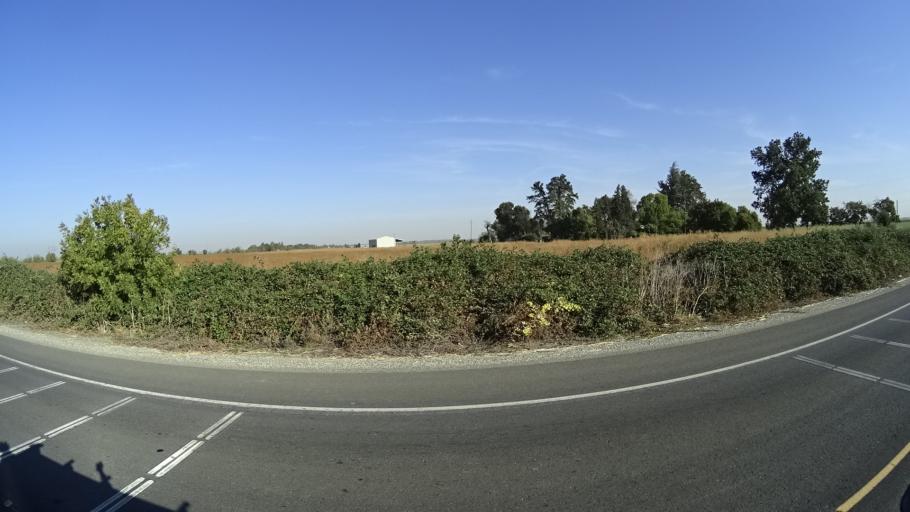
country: US
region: California
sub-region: Sacramento County
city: Parkway
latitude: 38.4141
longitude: -121.5797
